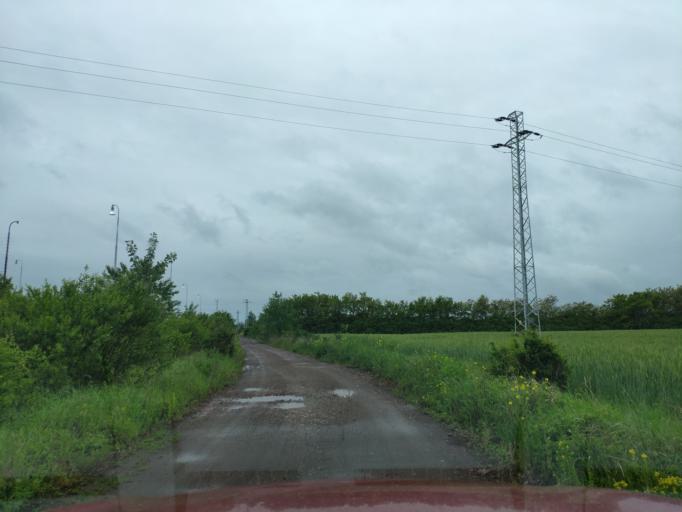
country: SK
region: Kosicky
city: Cierna nad Tisou
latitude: 48.4219
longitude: 22.0725
